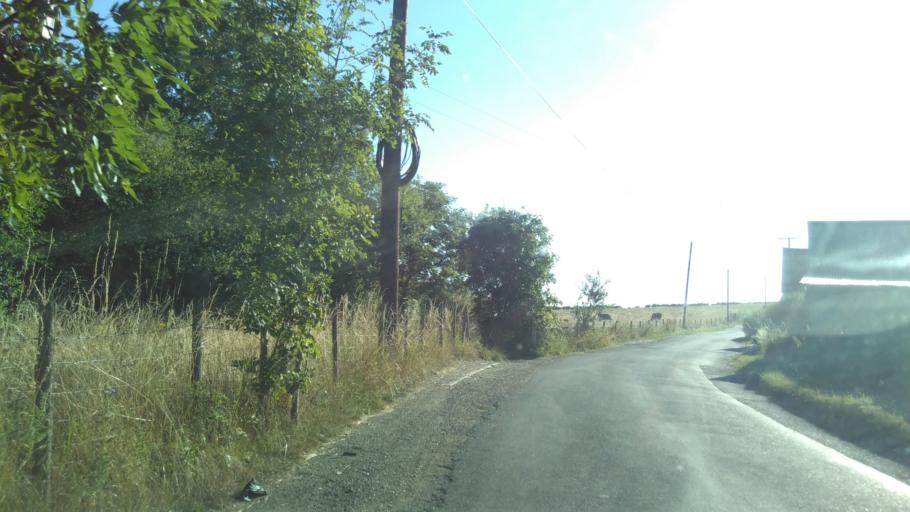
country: GB
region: England
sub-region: Kent
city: Dunkirk
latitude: 51.3101
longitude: 1.0072
